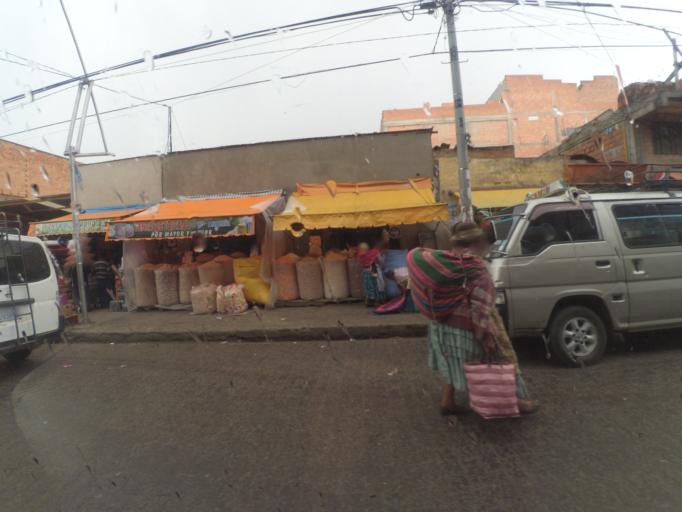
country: BO
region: La Paz
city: La Paz
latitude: -16.5090
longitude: -68.1630
